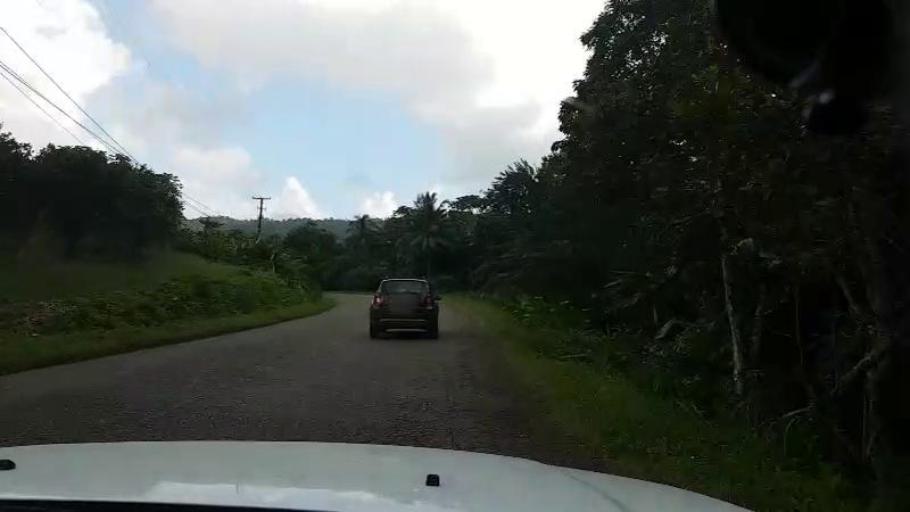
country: BZ
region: Stann Creek
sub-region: Dangriga
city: Dangriga
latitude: 17.0020
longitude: -88.4344
